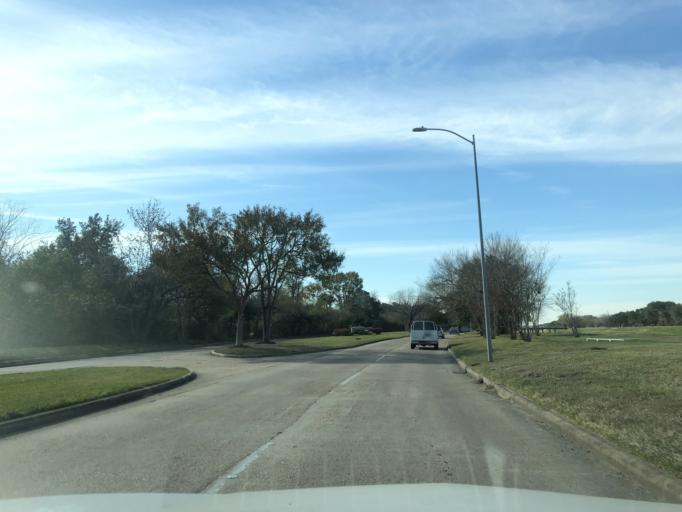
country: US
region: Texas
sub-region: Harris County
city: Bellaire
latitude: 29.6796
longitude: -95.4617
